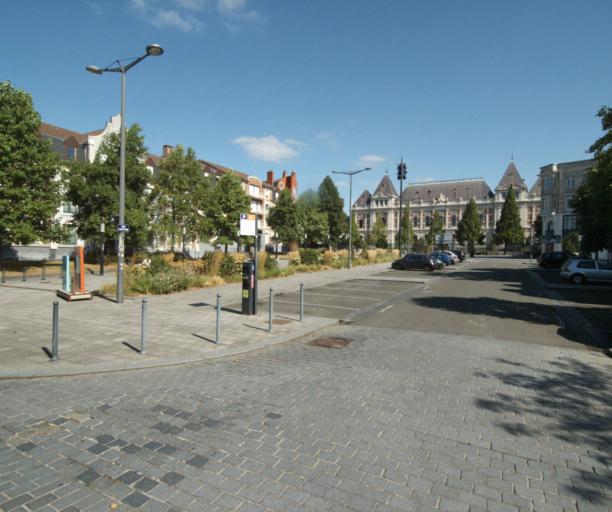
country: FR
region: Nord-Pas-de-Calais
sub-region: Departement du Nord
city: Roubaix
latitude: 50.6931
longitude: 3.1679
